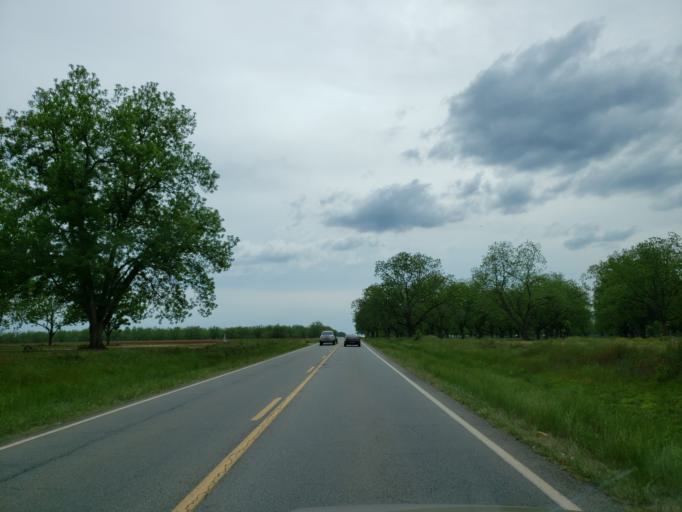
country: US
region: Georgia
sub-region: Houston County
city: Perry
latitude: 32.4370
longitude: -83.7973
